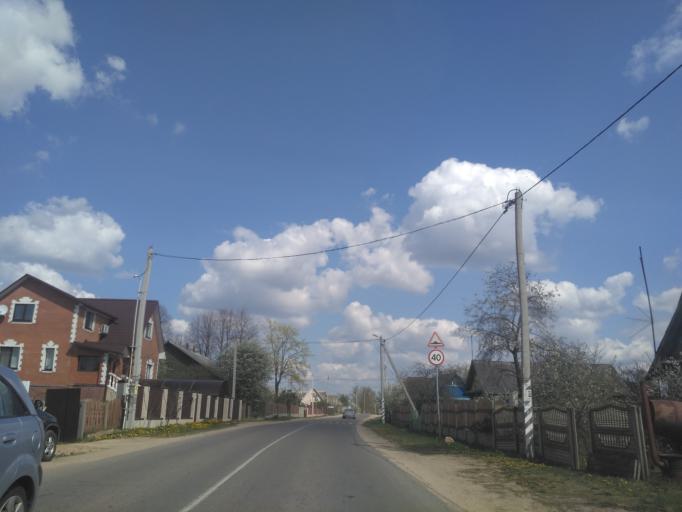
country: BY
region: Minsk
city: Radashkovichy
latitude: 54.1621
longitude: 27.2450
